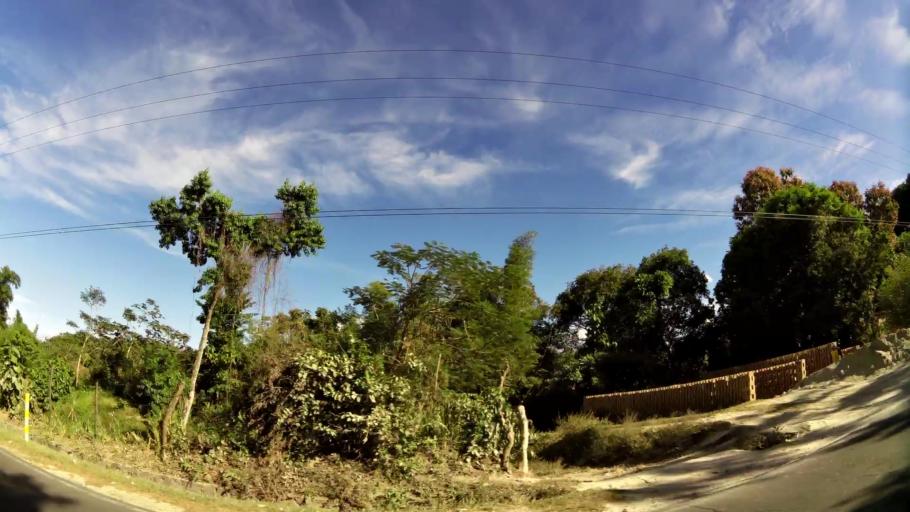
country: SV
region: Cuscatlan
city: Tecoluca
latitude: 13.8231
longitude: -89.0295
